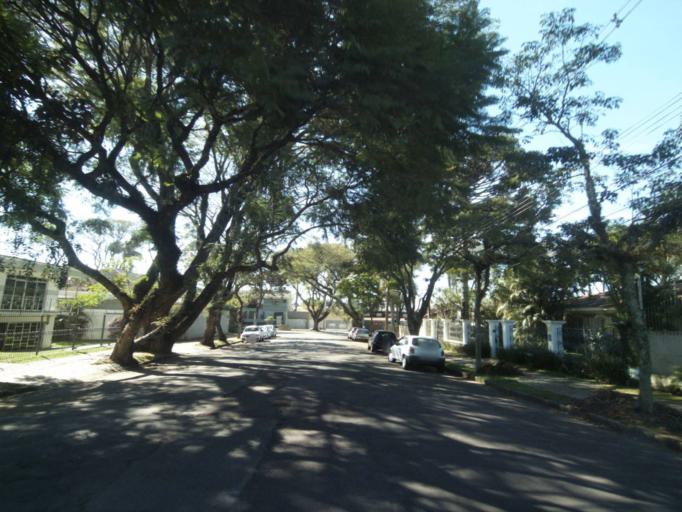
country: BR
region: Parana
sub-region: Curitiba
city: Curitiba
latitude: -25.4169
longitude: -49.2359
